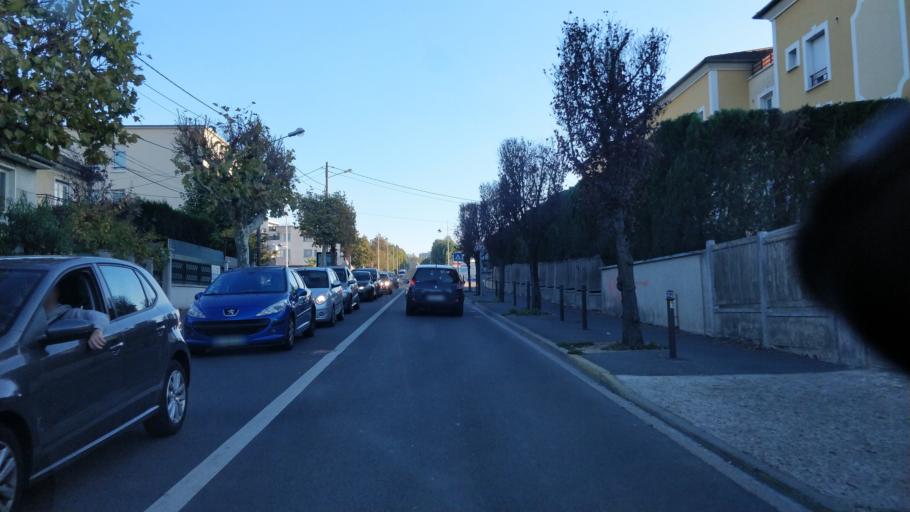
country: FR
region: Ile-de-France
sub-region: Departement de Seine-Saint-Denis
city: Gournay-sur-Marne
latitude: 48.8562
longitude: 2.5827
